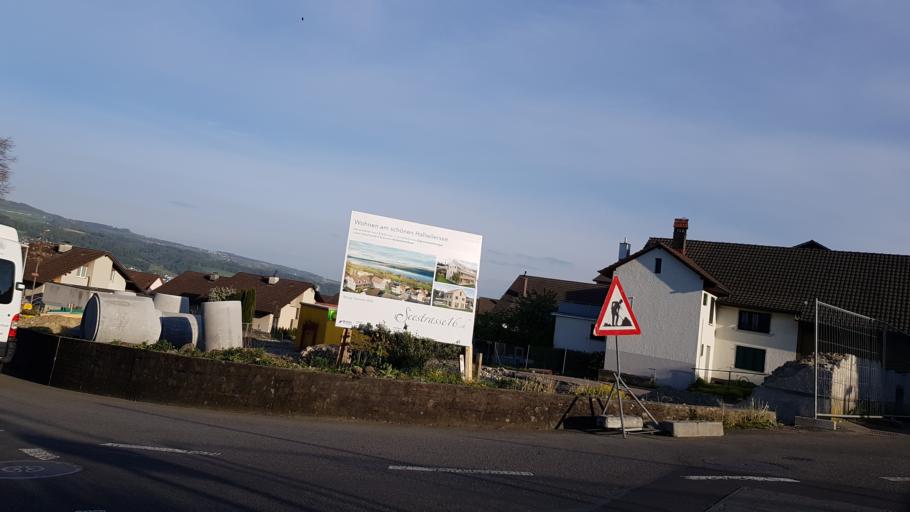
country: CH
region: Aargau
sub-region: Bezirk Kulm
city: Reinach
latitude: 47.2707
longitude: 8.2029
